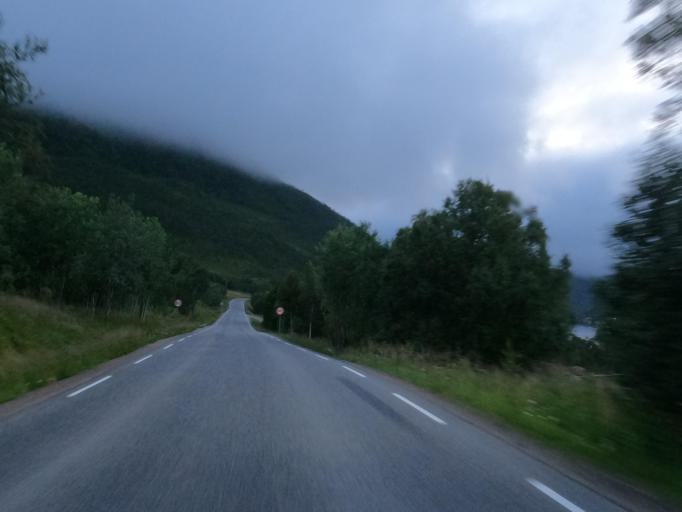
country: NO
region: Nordland
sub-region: Lodingen
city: Lodingen
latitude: 68.6024
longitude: 15.7863
